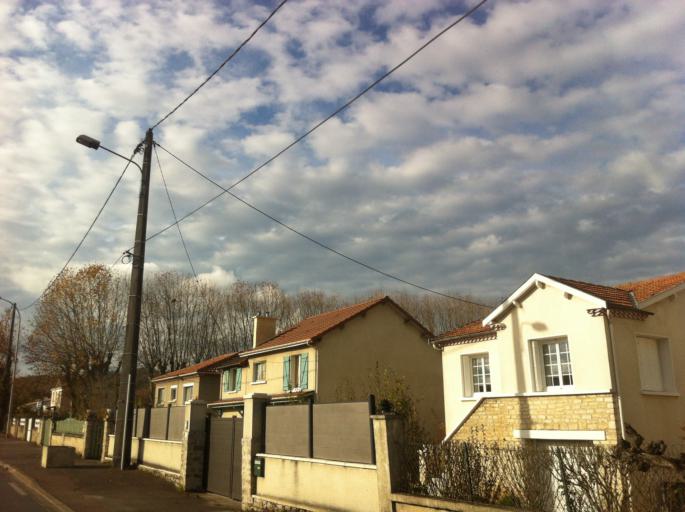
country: FR
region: Aquitaine
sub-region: Departement de la Dordogne
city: Trelissac
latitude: 45.1891
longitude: 0.7553
